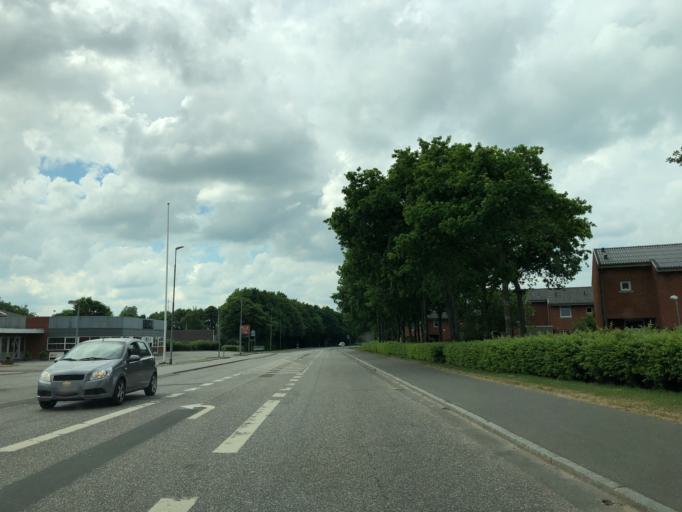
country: DK
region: Central Jutland
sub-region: Struer Kommune
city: Struer
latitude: 56.4824
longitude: 8.5902
